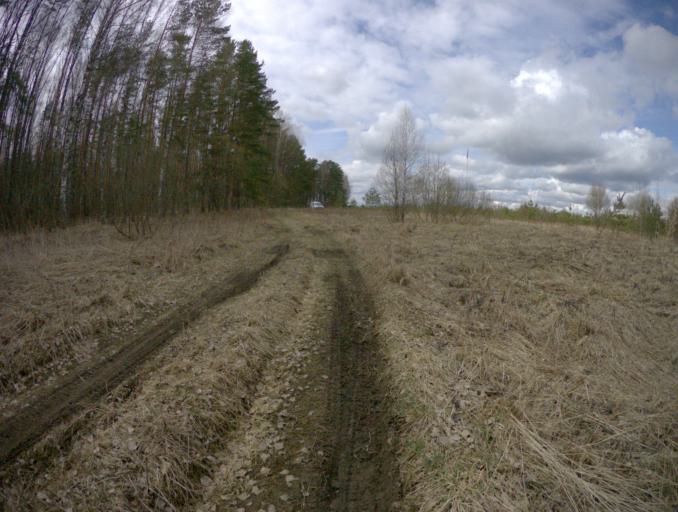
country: RU
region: Vladimir
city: Orgtrud
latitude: 56.0646
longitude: 40.6913
